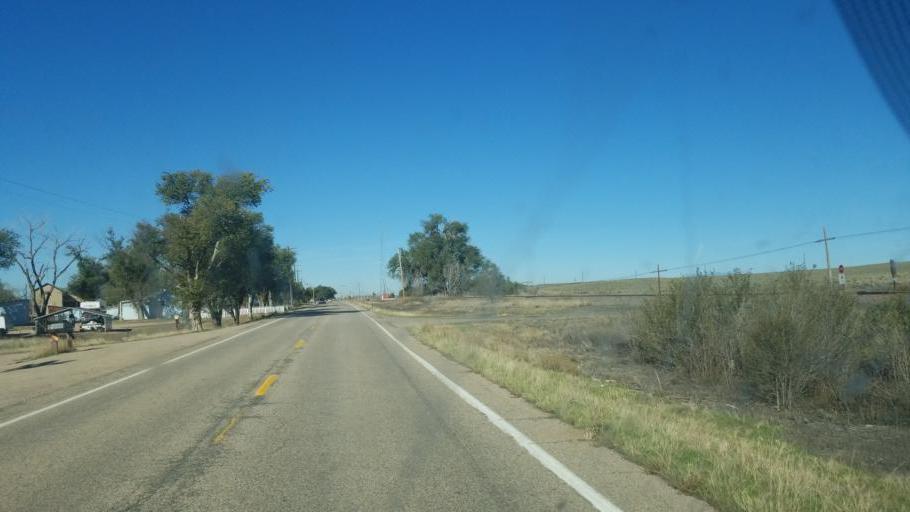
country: US
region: Colorado
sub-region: Pueblo County
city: Pueblo
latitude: 38.2603
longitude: -104.3421
